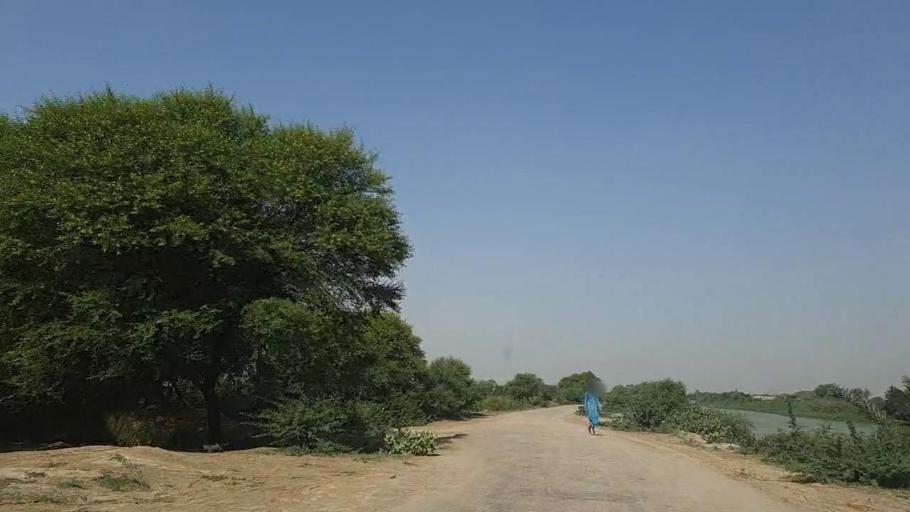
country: PK
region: Sindh
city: Daro Mehar
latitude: 24.7232
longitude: 68.1566
